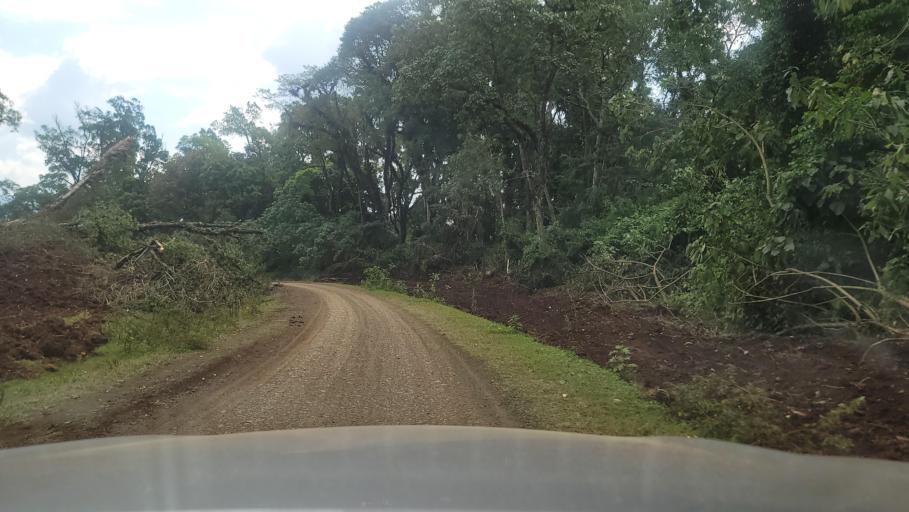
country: ET
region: Southern Nations, Nationalities, and People's Region
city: Bonga
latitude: 7.6643
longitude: 36.2433
